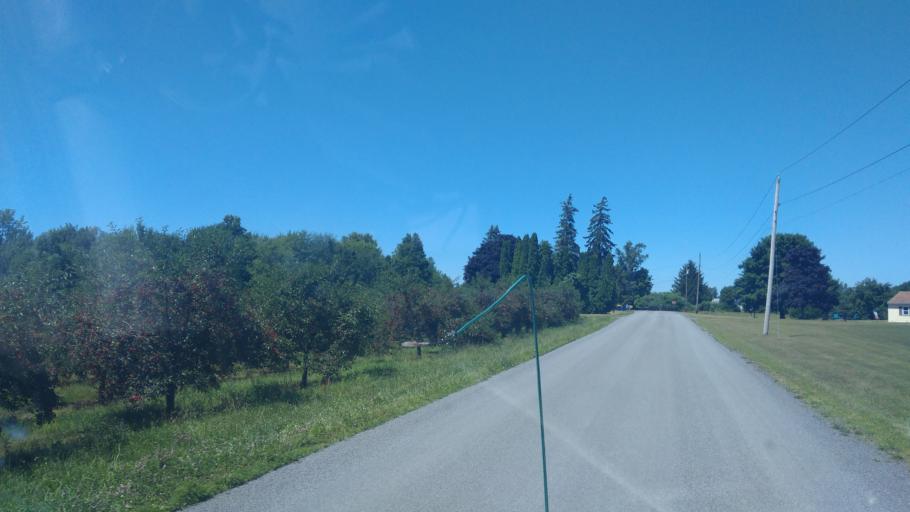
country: US
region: New York
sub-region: Wayne County
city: Lyons
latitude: 43.1658
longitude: -76.9776
